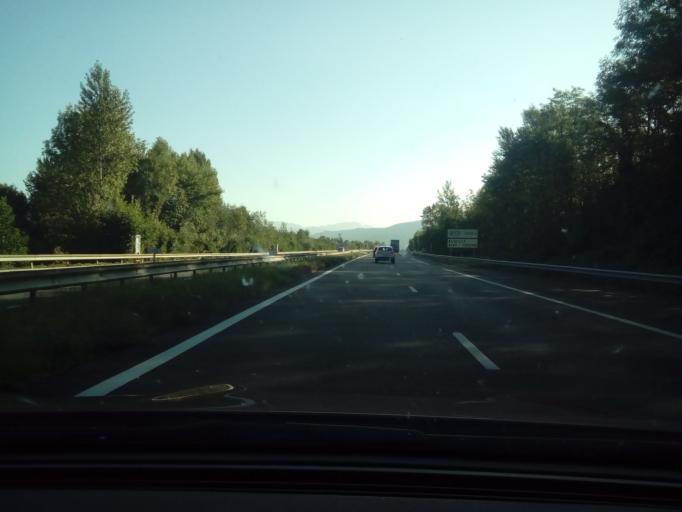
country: FR
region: Rhone-Alpes
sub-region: Departement de la Haute-Savoie
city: Alby-sur-Cheran
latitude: 45.8131
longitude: 5.9943
